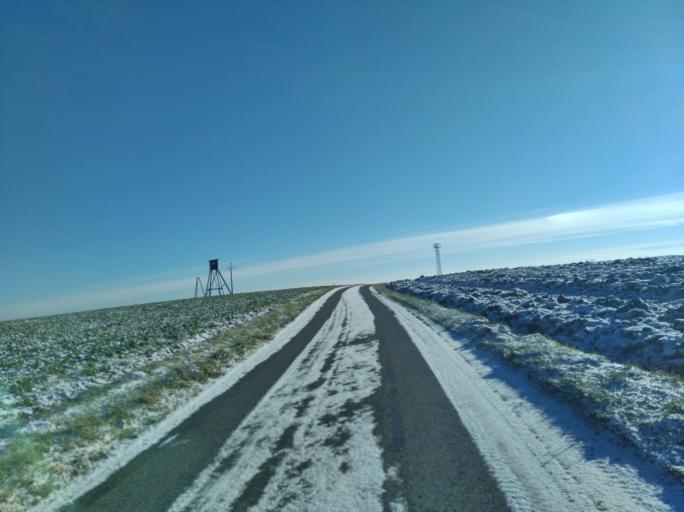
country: PL
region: Subcarpathian Voivodeship
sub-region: Powiat ropczycko-sedziszowski
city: Iwierzyce
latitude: 49.9527
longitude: 21.7599
